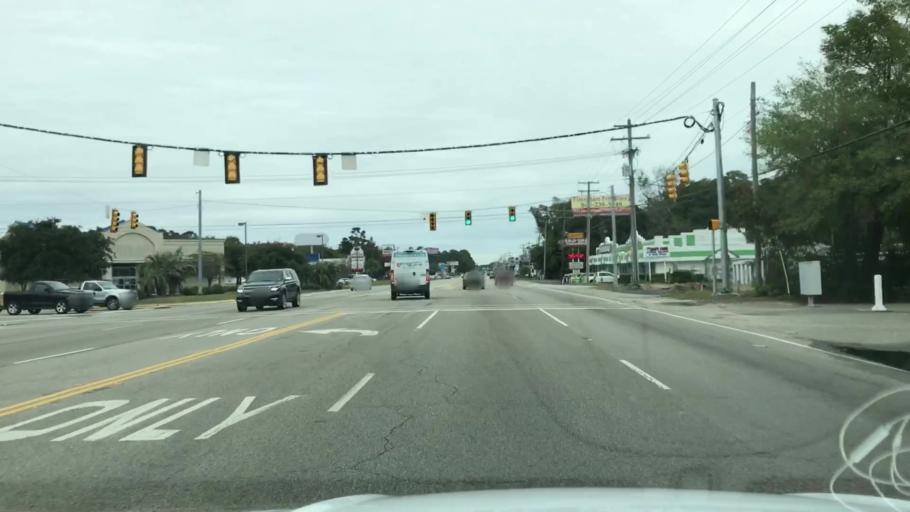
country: US
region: South Carolina
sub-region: Horry County
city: Garden City
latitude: 33.5789
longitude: -79.0220
